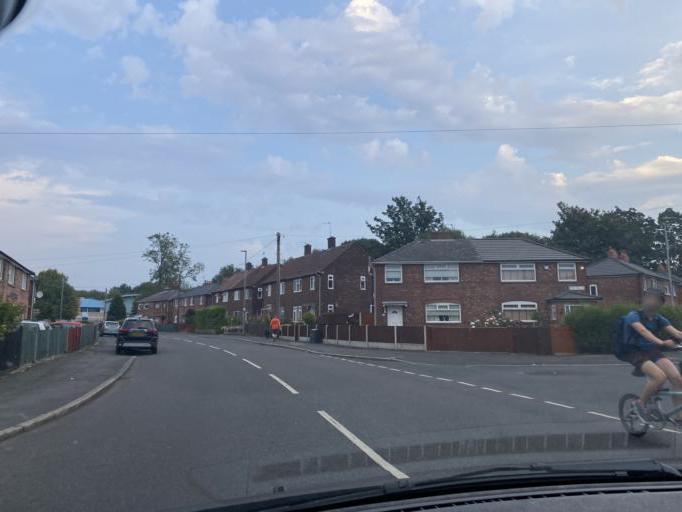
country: GB
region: England
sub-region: Manchester
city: Fallowfield
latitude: 53.4467
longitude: -2.2303
